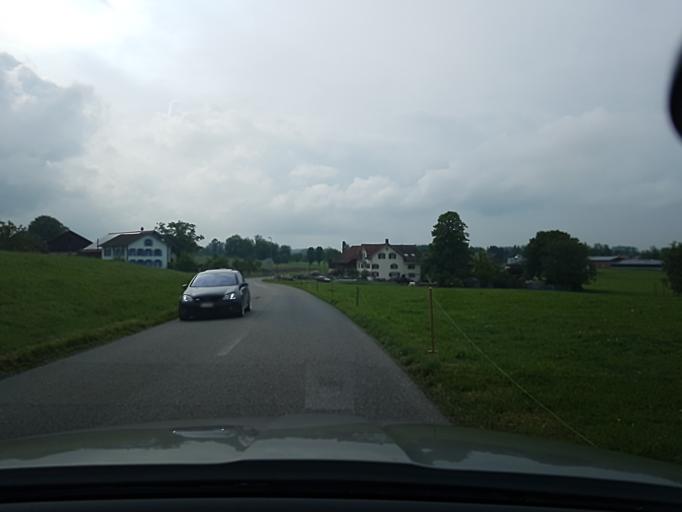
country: CH
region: Thurgau
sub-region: Arbon District
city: Roggwil
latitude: 47.5075
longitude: 9.3833
